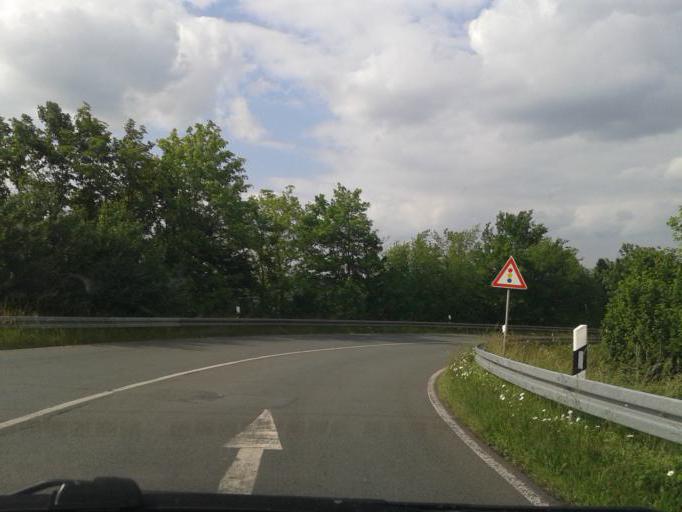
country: DE
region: North Rhine-Westphalia
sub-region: Regierungsbezirk Detmold
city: Paderborn
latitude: 51.7409
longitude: 8.7312
